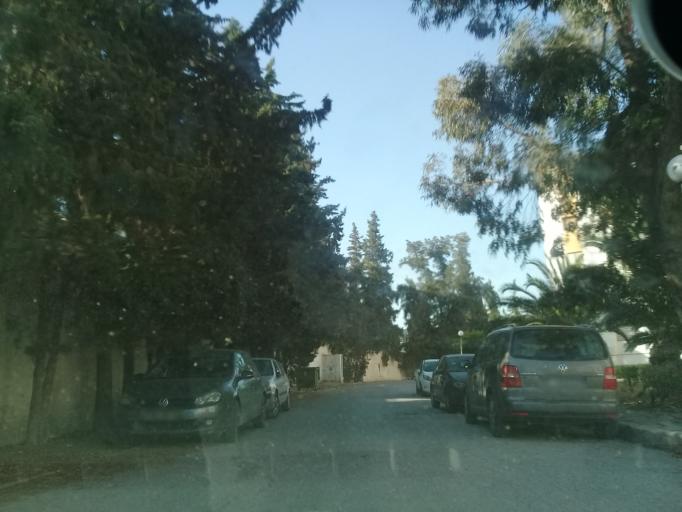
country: TN
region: Ariana
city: Ariana
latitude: 36.8378
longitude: 10.1910
